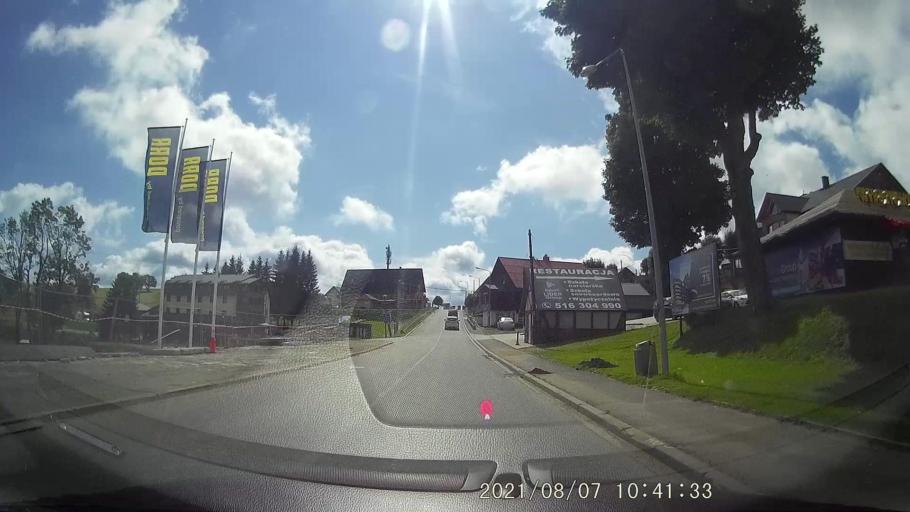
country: PL
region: Lower Silesian Voivodeship
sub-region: Powiat klodzki
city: Duszniki-Zdroj
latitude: 50.3370
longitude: 16.3864
